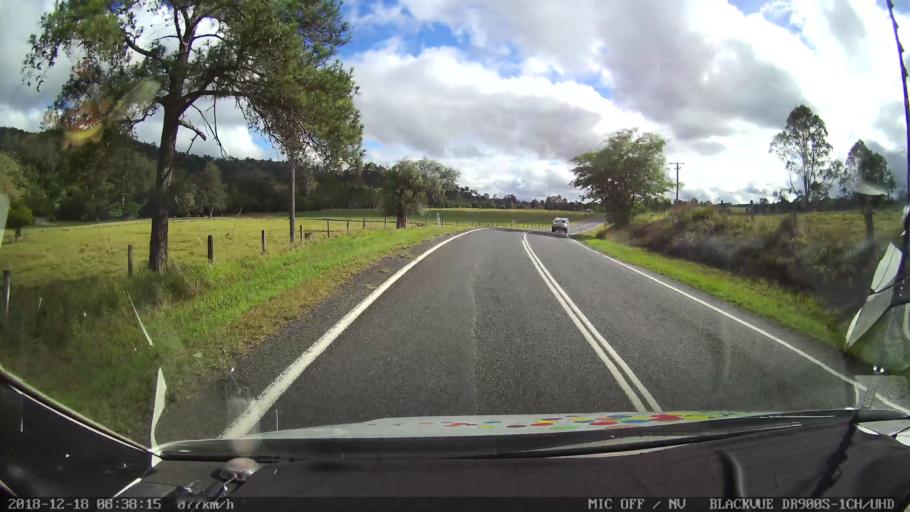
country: AU
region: New South Wales
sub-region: Kyogle
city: Kyogle
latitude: -28.2570
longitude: 152.8260
